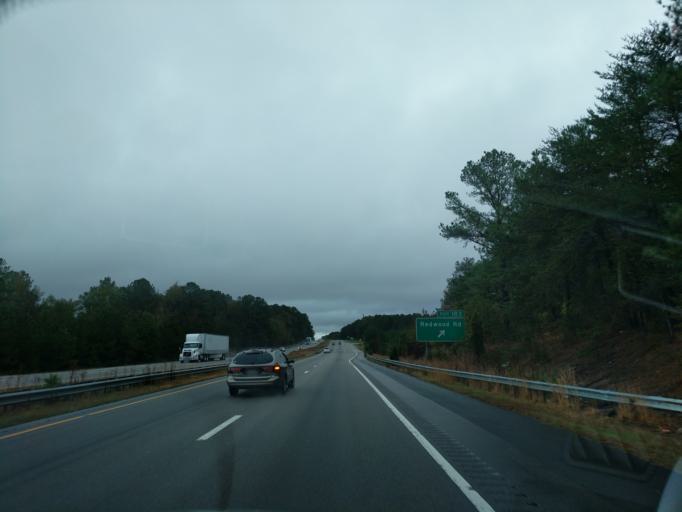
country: US
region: North Carolina
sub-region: Durham County
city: Gorman
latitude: 36.0566
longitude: -78.7974
